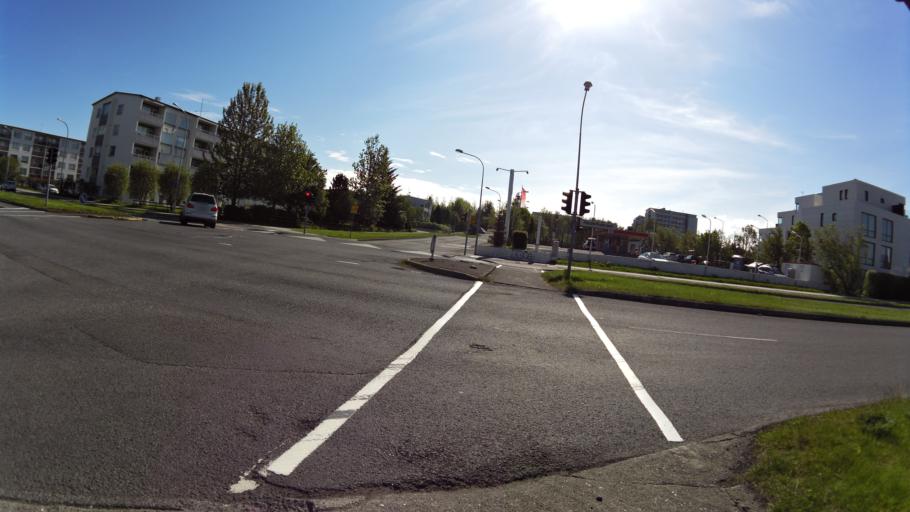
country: IS
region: Capital Region
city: Reykjavik
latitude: 64.1266
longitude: -21.8877
